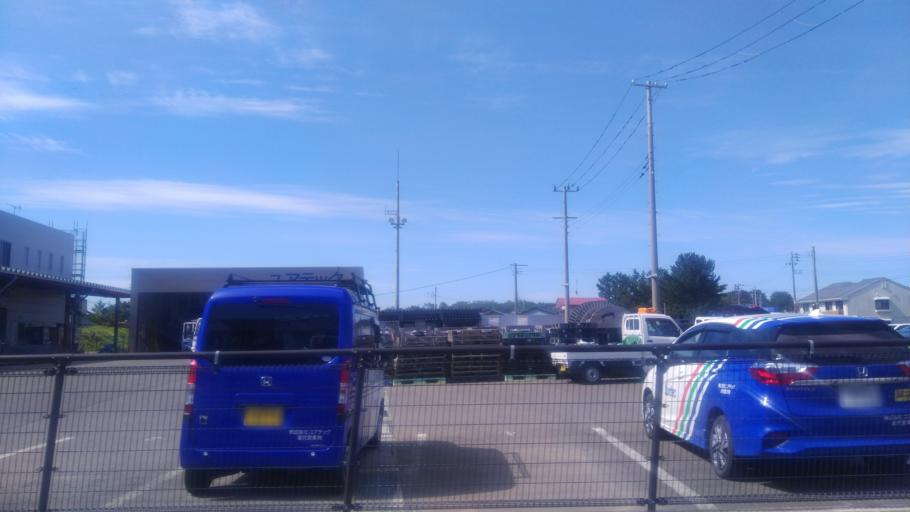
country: JP
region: Akita
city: Noshiromachi
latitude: 40.1961
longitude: 140.0226
